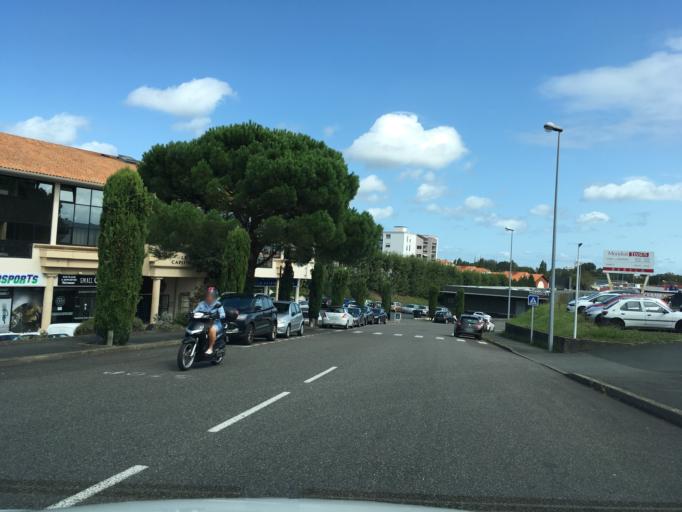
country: FR
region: Aquitaine
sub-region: Departement des Pyrenees-Atlantiques
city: Anglet
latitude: 43.4879
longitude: -1.5037
